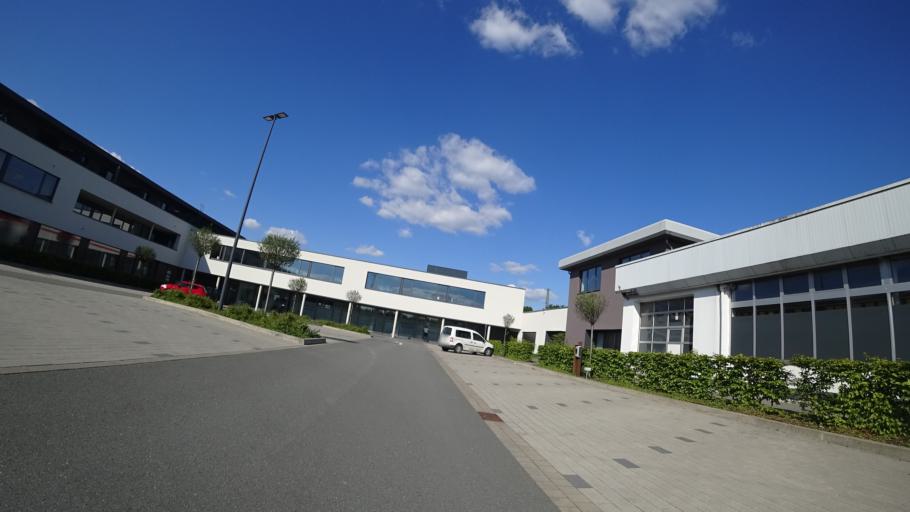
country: DE
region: North Rhine-Westphalia
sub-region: Regierungsbezirk Detmold
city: Guetersloh
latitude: 51.8945
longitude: 8.3650
